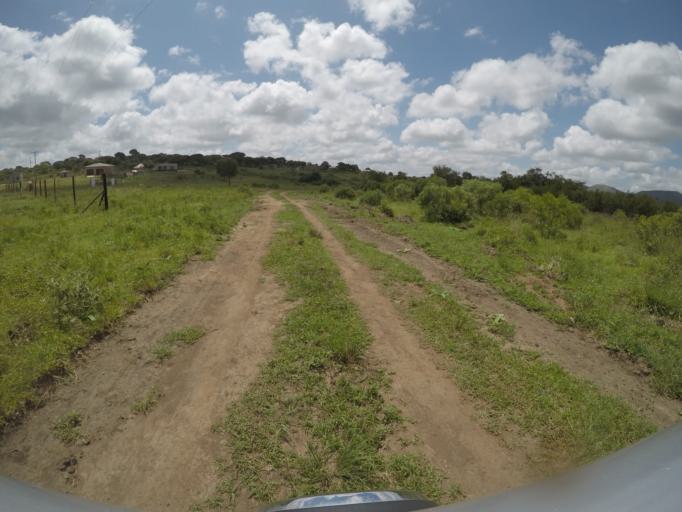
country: ZA
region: KwaZulu-Natal
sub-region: uThungulu District Municipality
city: Empangeni
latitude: -28.5895
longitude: 31.8393
